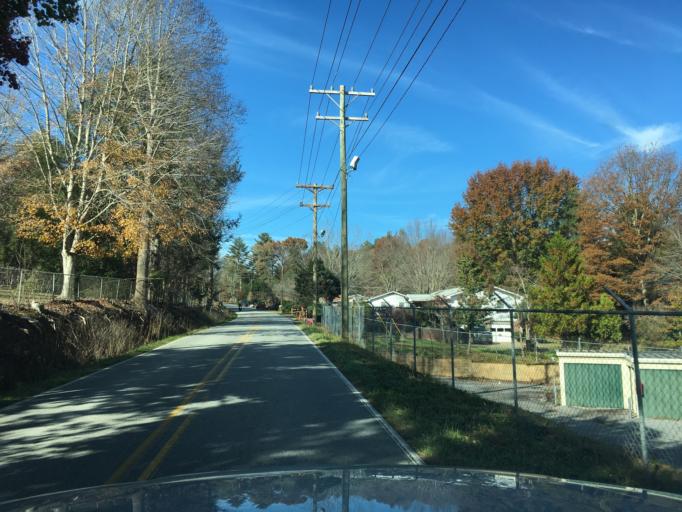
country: US
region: North Carolina
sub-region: Henderson County
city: Etowah
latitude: 35.3011
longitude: -82.6271
